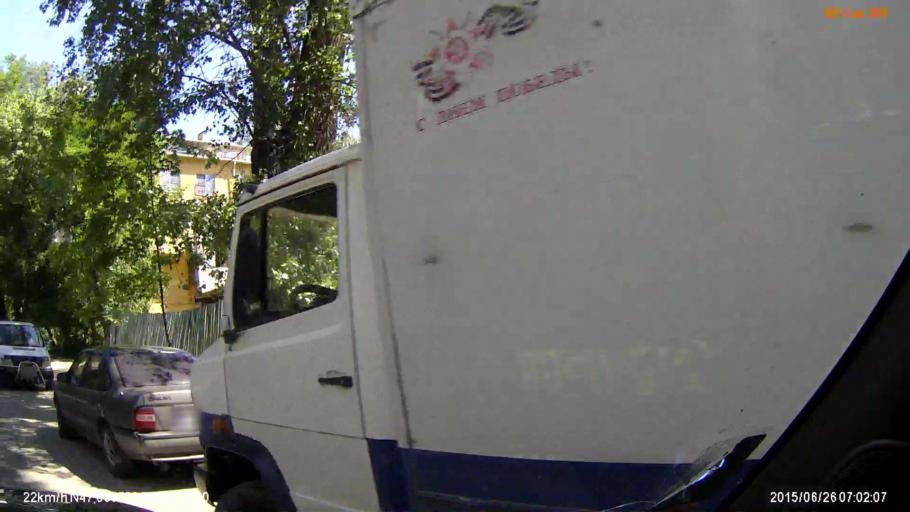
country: MD
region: Chisinau
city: Chisinau
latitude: 47.0367
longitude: 28.8653
